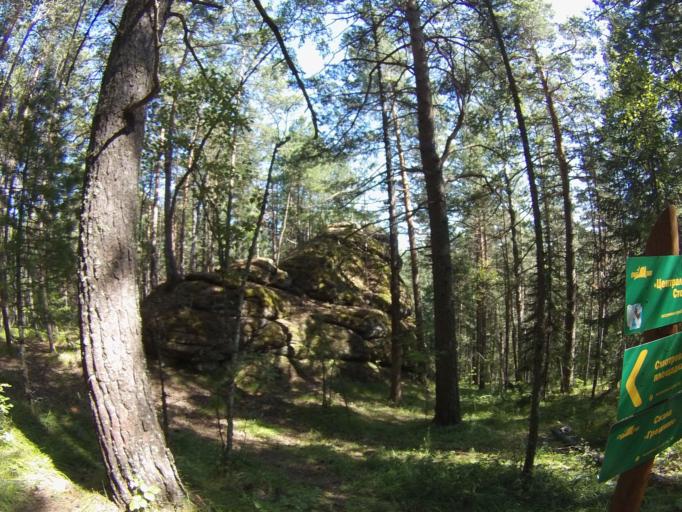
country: RU
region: Krasnoyarskiy
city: Krasnoyarsk
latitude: 55.9318
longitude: 92.7605
